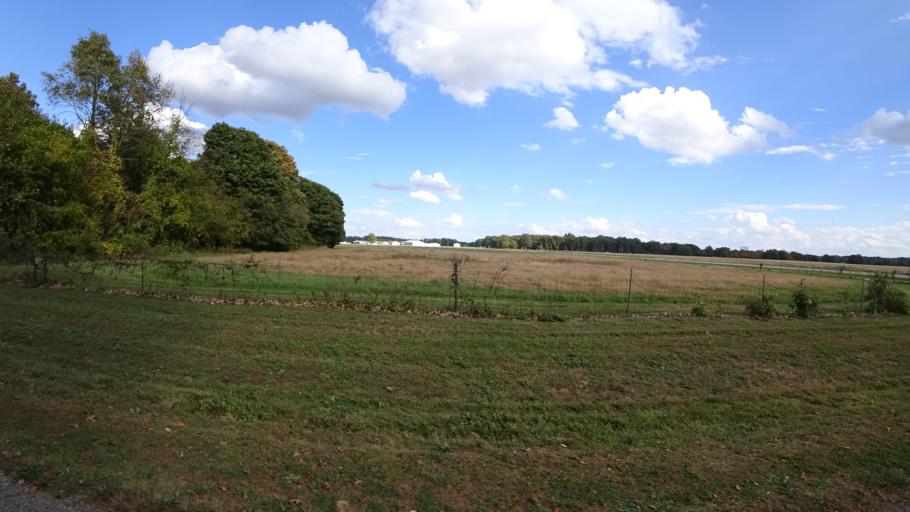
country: US
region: Michigan
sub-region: Saint Joseph County
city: Three Rivers
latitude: 41.9554
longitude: -85.5978
